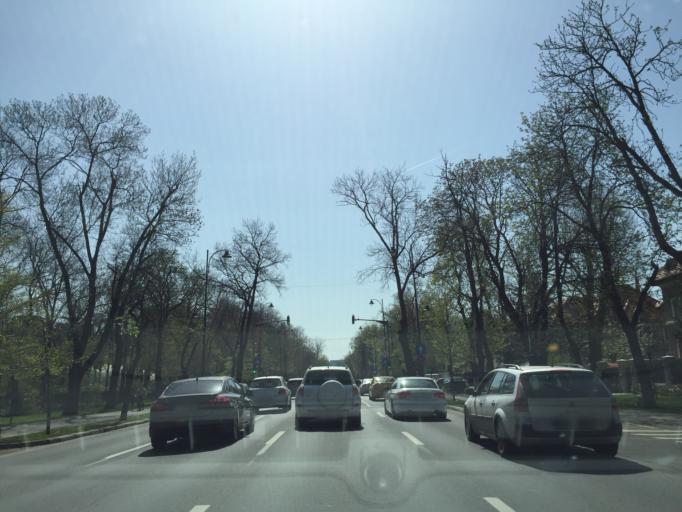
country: RO
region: Bucuresti
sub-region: Municipiul Bucuresti
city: Bucuresti
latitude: 44.4634
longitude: 26.0800
